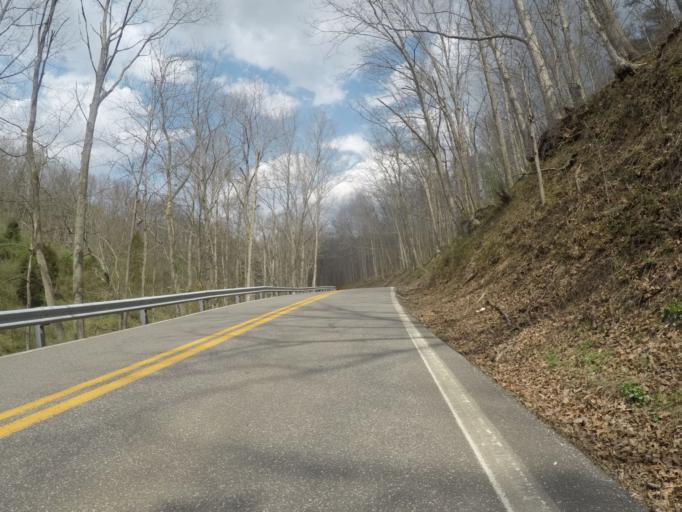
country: US
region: West Virginia
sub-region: Cabell County
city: Pea Ridge
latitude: 38.3483
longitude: -82.3360
